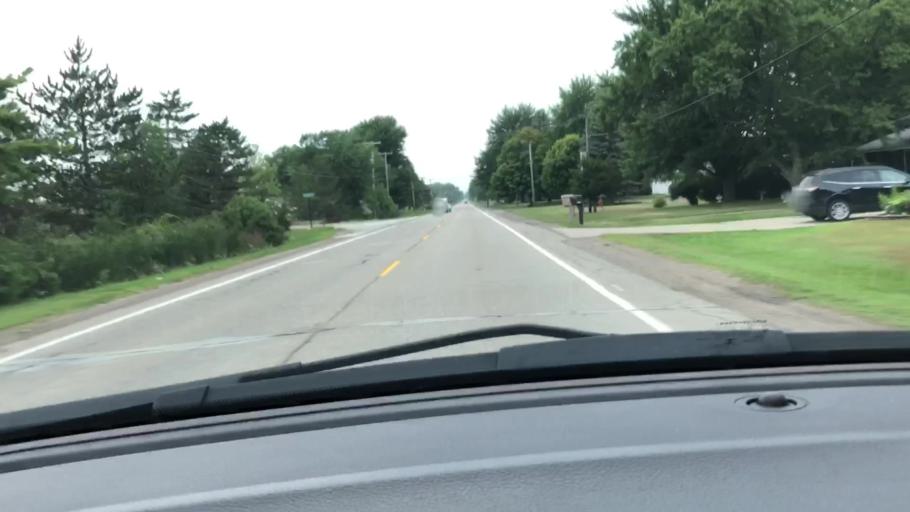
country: US
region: Michigan
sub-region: Bay County
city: Auburn
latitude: 43.6041
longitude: -84.1189
